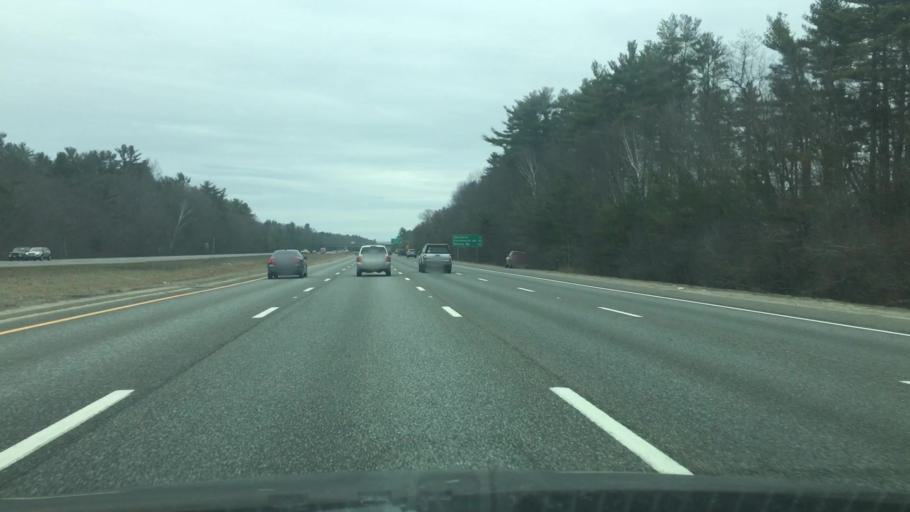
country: US
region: Massachusetts
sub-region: Essex County
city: Boxford
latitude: 42.6430
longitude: -70.9767
